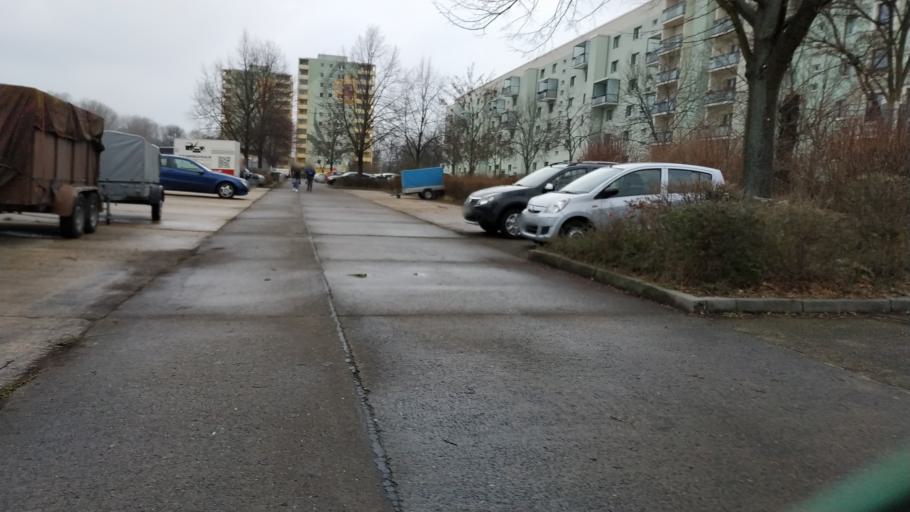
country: DE
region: Berlin
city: Marzahn
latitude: 52.5439
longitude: 13.5844
